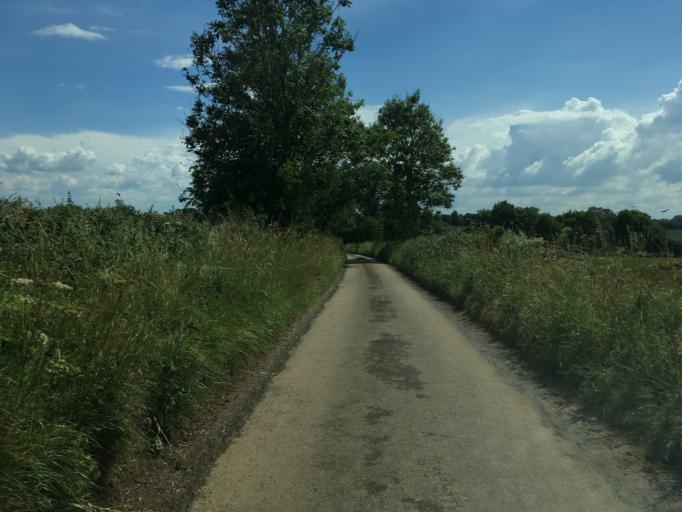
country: GB
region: England
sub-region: Gloucestershire
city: Tetbury
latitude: 51.6450
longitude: -2.1758
